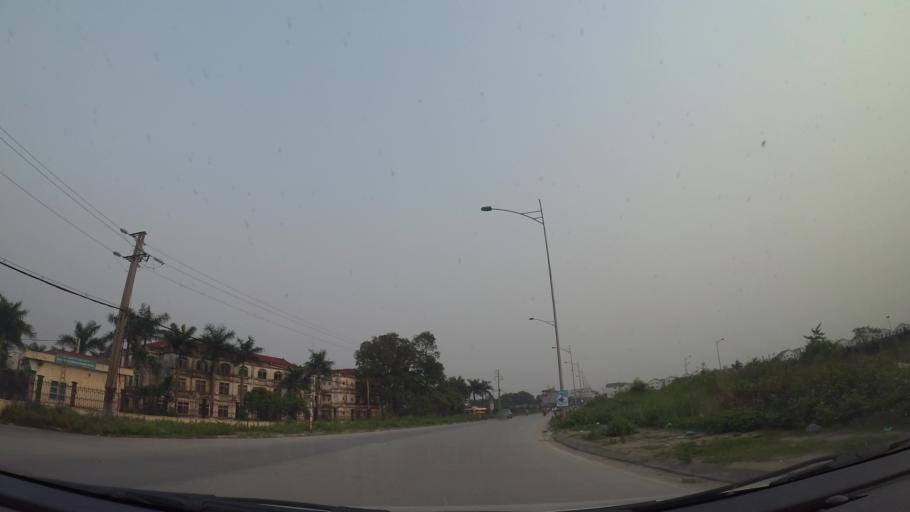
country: VN
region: Ha Noi
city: Cau Dien
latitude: 21.0018
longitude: 105.7238
